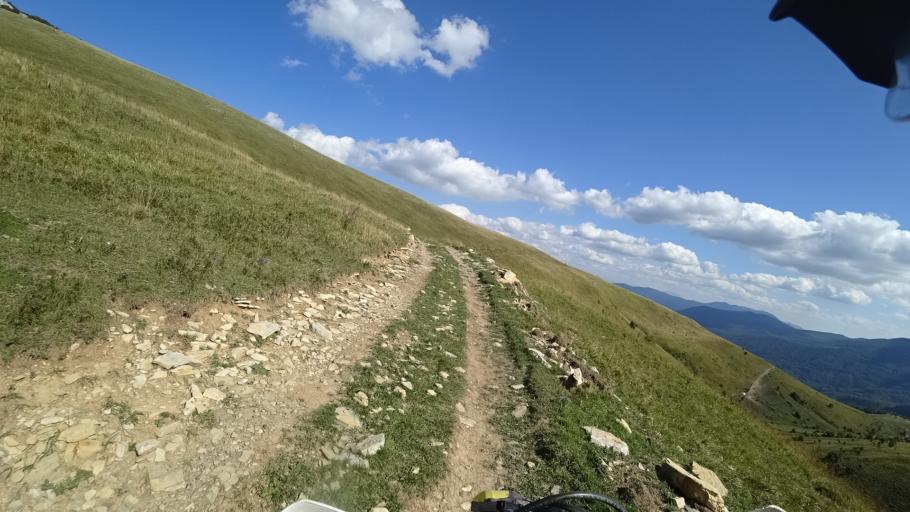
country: HR
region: Zadarska
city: Gracac
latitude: 44.3969
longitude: 16.0156
